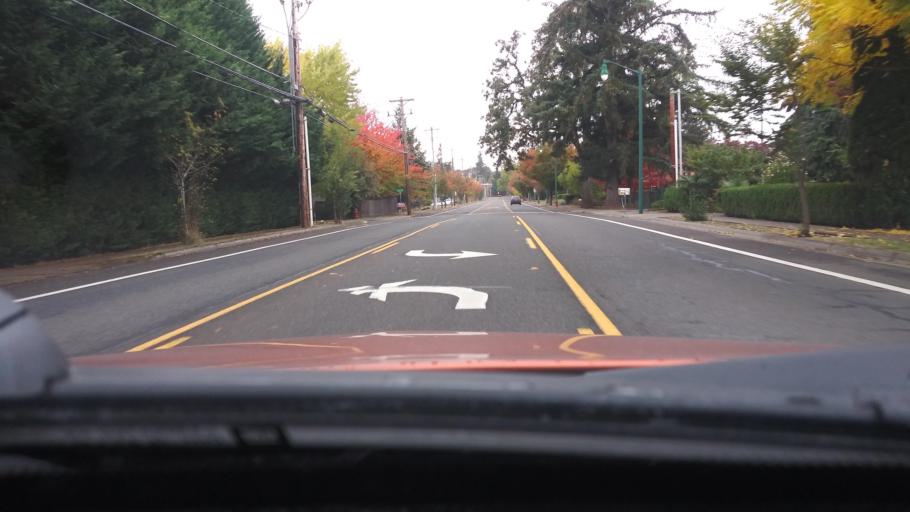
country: US
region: Oregon
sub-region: Washington County
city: Forest Grove
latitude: 45.5280
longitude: -123.1078
